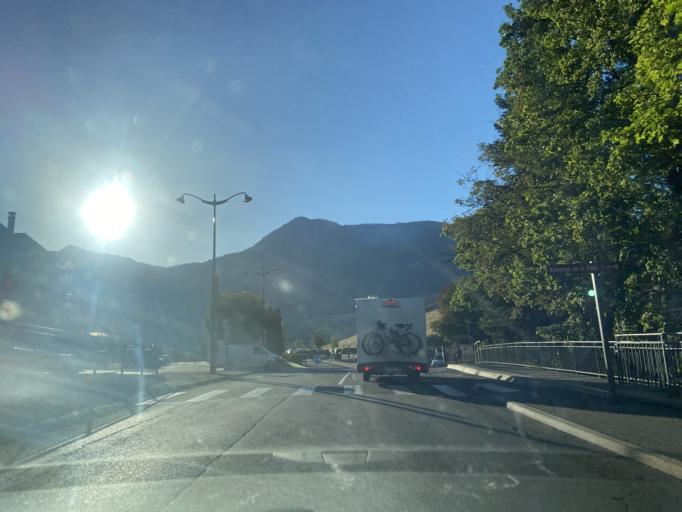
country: FR
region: Provence-Alpes-Cote d'Azur
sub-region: Departement des Hautes-Alpes
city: Briancon
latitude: 44.9016
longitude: 6.6429
